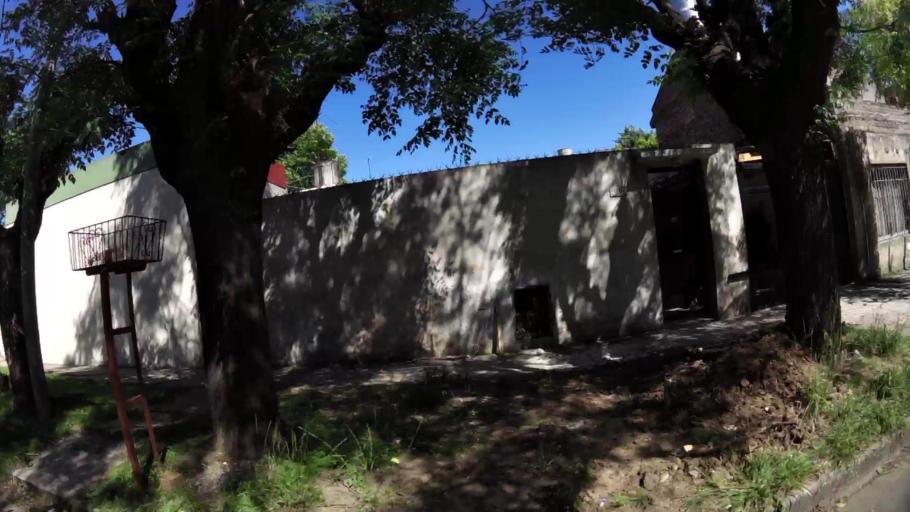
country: AR
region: Buenos Aires
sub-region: Partido de General San Martin
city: General San Martin
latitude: -34.5474
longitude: -58.5652
